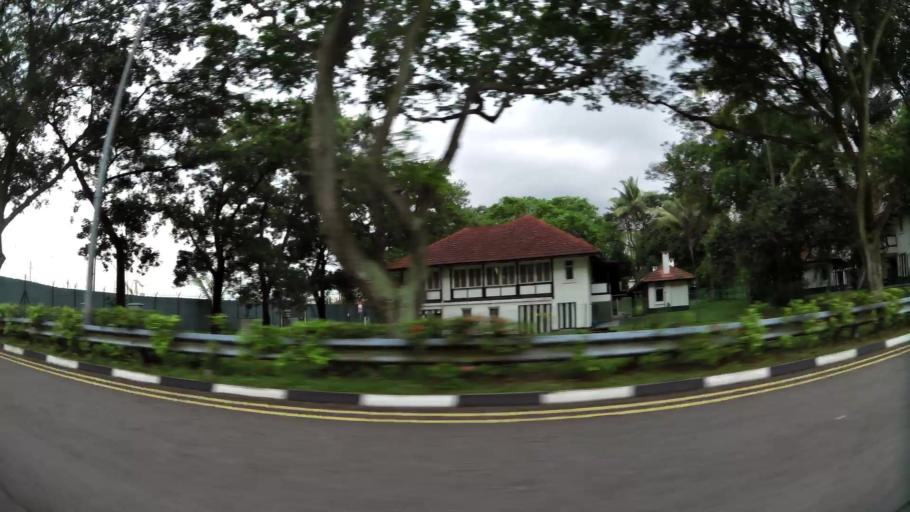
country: MY
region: Johor
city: Kampung Pasir Gudang Baru
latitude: 1.4596
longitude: 103.8273
